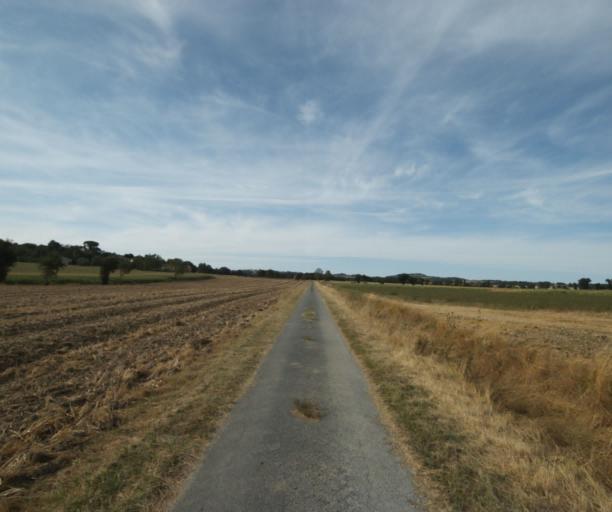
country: FR
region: Midi-Pyrenees
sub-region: Departement du Tarn
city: Puylaurens
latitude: 43.5210
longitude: 2.0290
